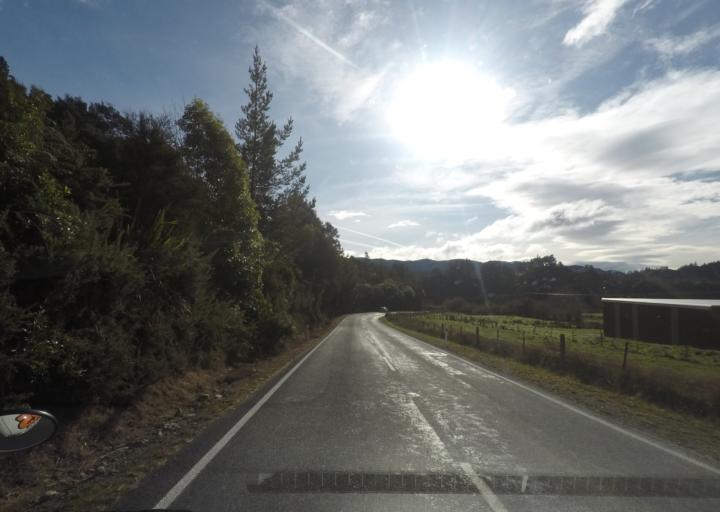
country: NZ
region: Tasman
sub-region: Tasman District
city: Motueka
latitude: -41.0195
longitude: 172.9806
